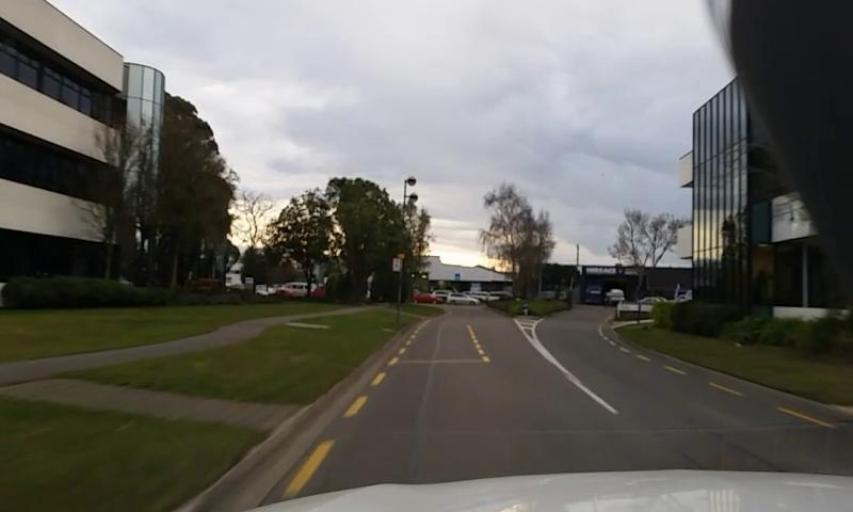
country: NZ
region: Canterbury
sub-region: Christchurch City
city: Christchurch
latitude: -43.4923
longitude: 172.5610
